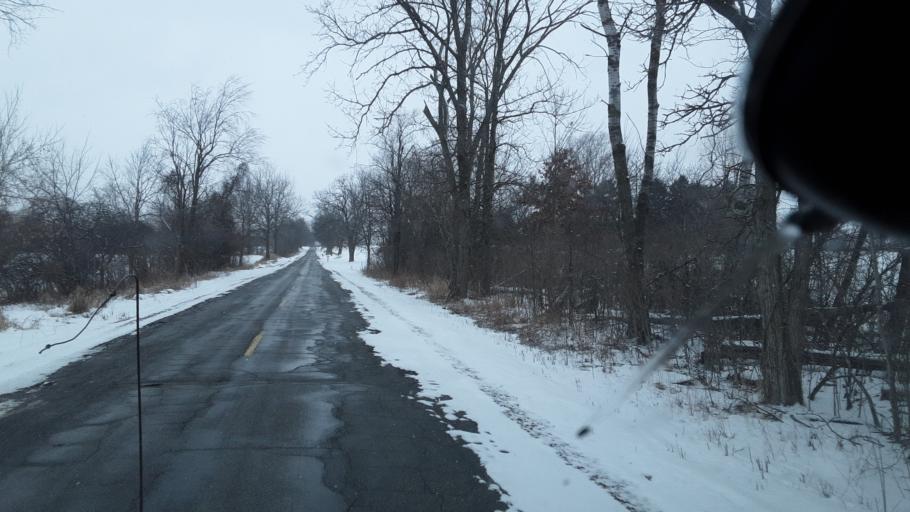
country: US
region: Michigan
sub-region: Ingham County
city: Leslie
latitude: 42.4367
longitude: -84.4555
